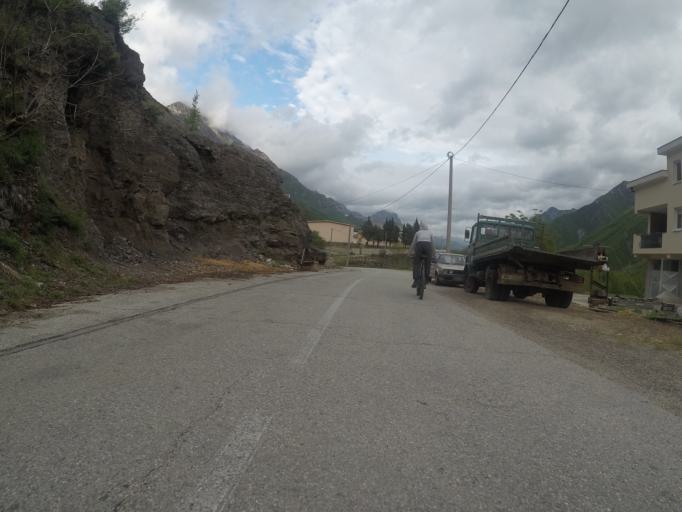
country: BA
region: Federation of Bosnia and Herzegovina
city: Siroki Brijeg
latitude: 43.5420
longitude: 17.5641
